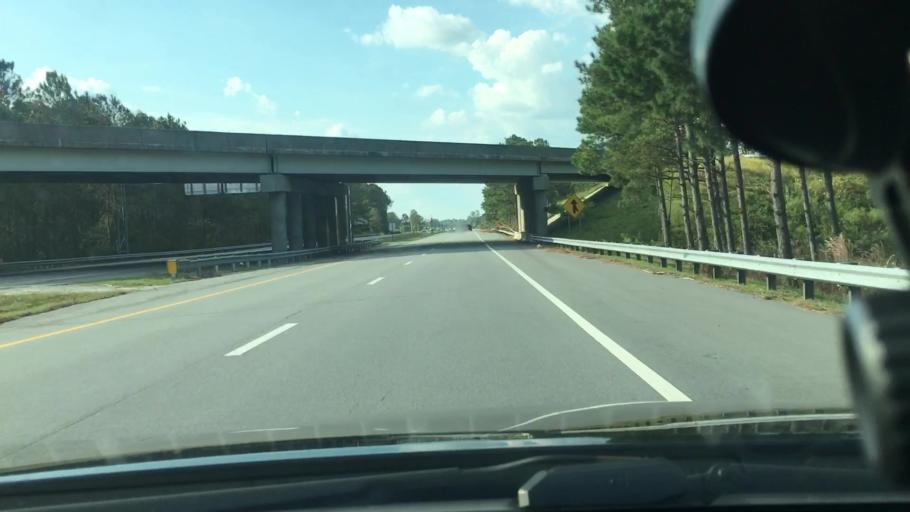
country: US
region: North Carolina
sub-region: Craven County
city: New Bern
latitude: 35.1147
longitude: -77.0121
